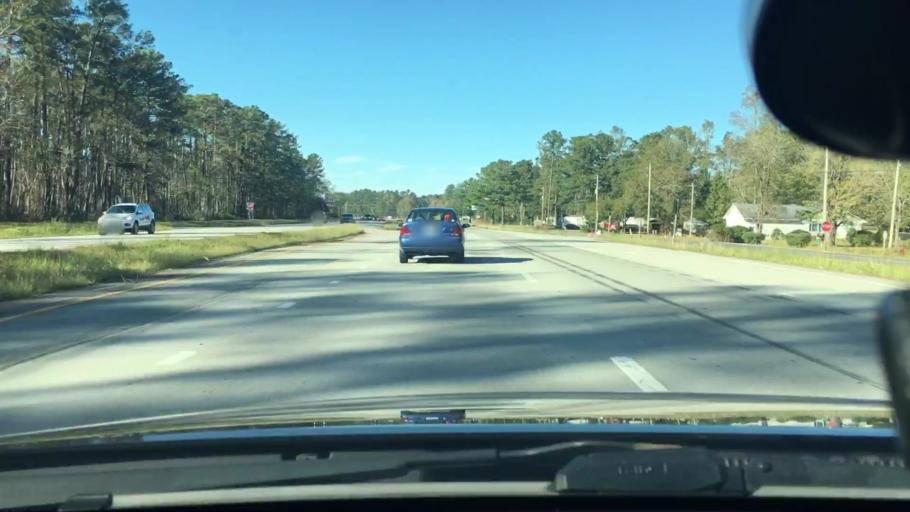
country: US
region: North Carolina
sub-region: Craven County
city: Neuse Forest
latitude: 34.9470
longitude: -76.9483
